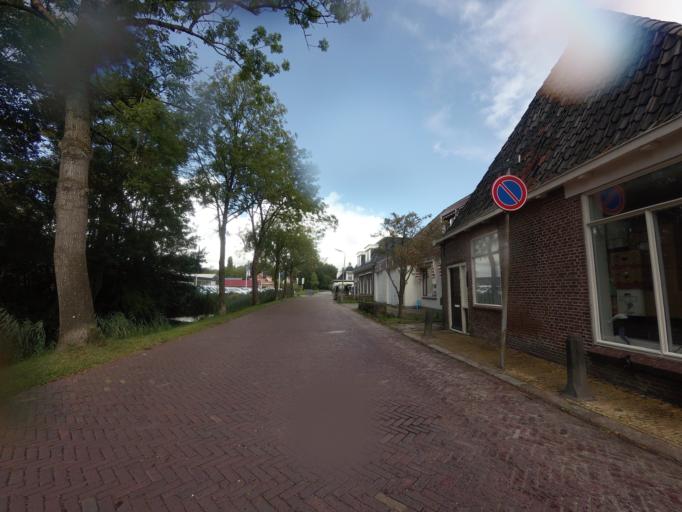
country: NL
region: Friesland
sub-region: Gemeente Leeuwarden
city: Wirdum
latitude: 53.1495
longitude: 5.8015
